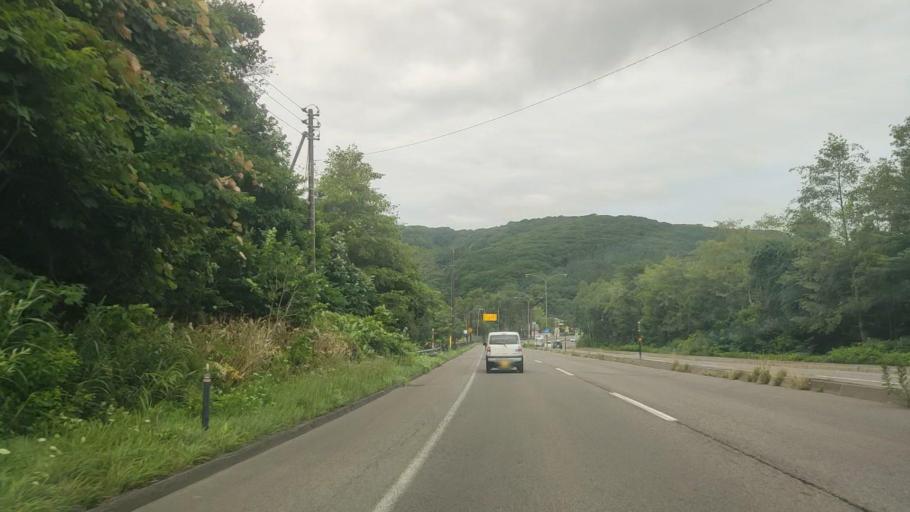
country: JP
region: Hokkaido
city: Nanae
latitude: 41.9585
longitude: 140.6493
